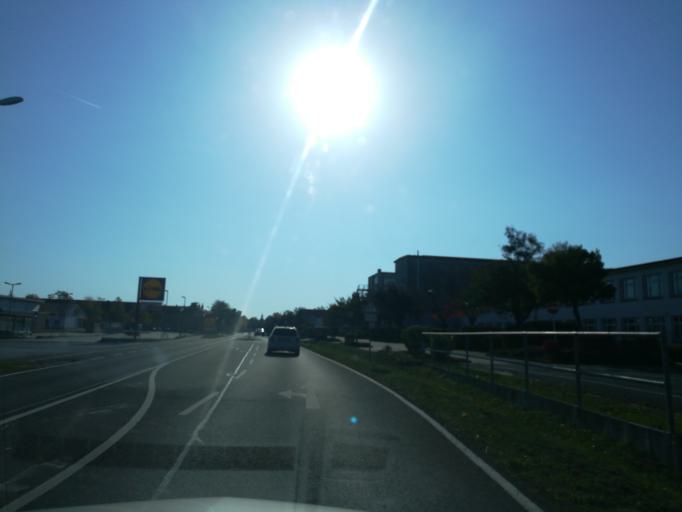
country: DE
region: Saxony-Anhalt
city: Gommern
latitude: 52.0782
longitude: 11.8201
